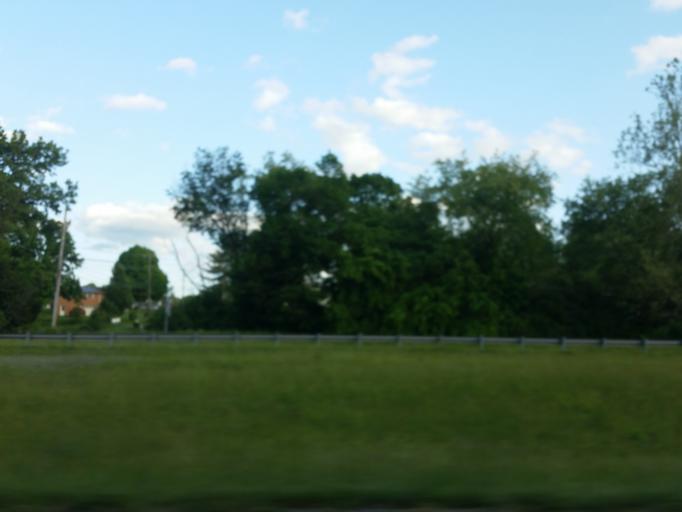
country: US
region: Virginia
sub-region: Washington County
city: Abingdon
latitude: 36.6544
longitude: -82.0767
